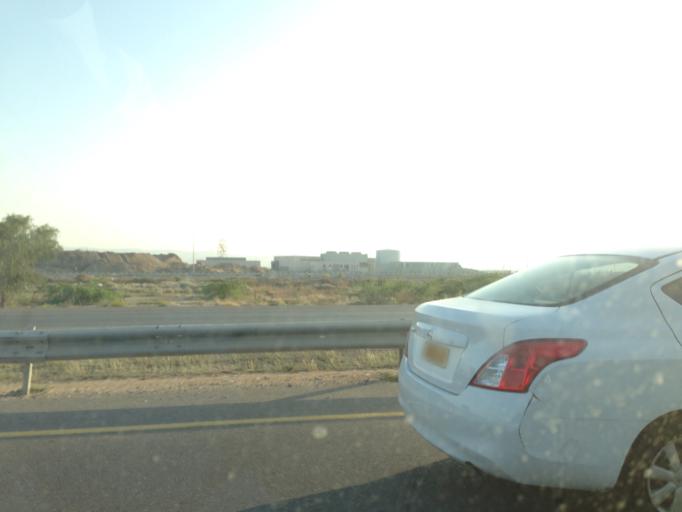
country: OM
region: Muhafazat Masqat
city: As Sib al Jadidah
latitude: 23.6196
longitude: 58.2756
